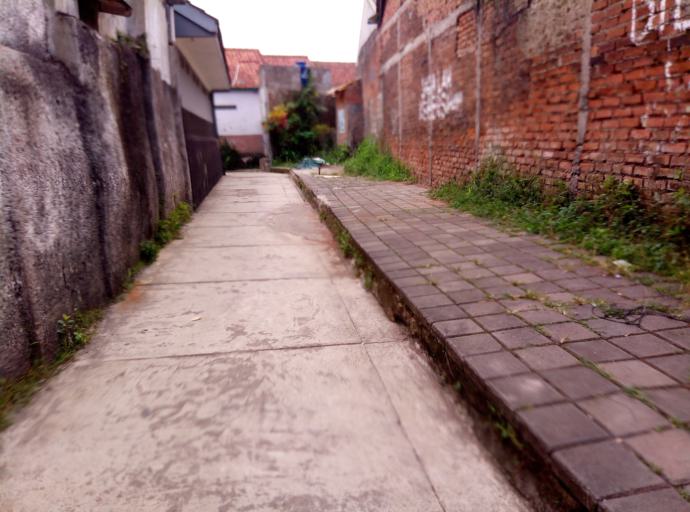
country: ID
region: West Java
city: Bandung
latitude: -6.9285
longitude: 107.6468
